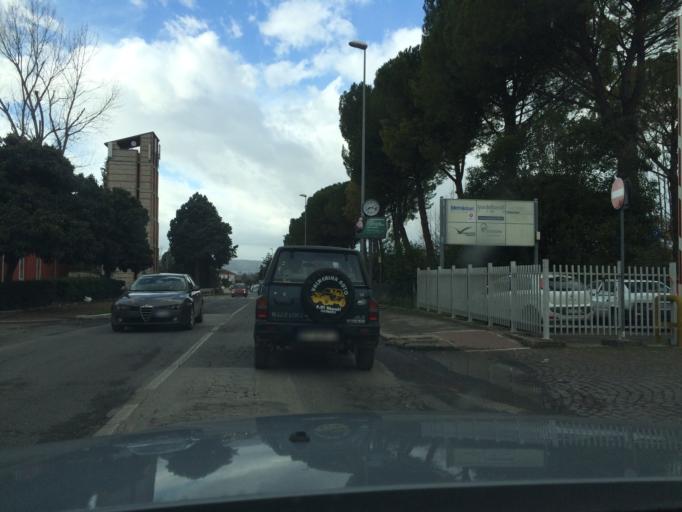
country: IT
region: Umbria
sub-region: Provincia di Terni
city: Terni
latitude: 42.5475
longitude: 12.6177
